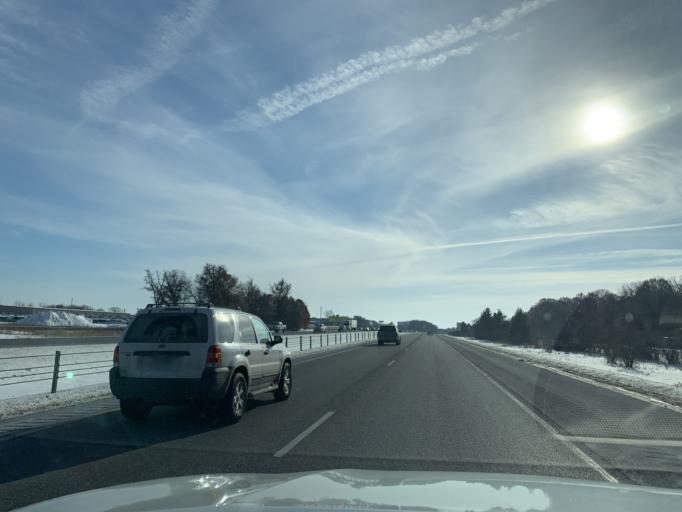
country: US
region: Minnesota
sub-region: Chisago County
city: Wyoming
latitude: 45.3294
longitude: -93.0046
